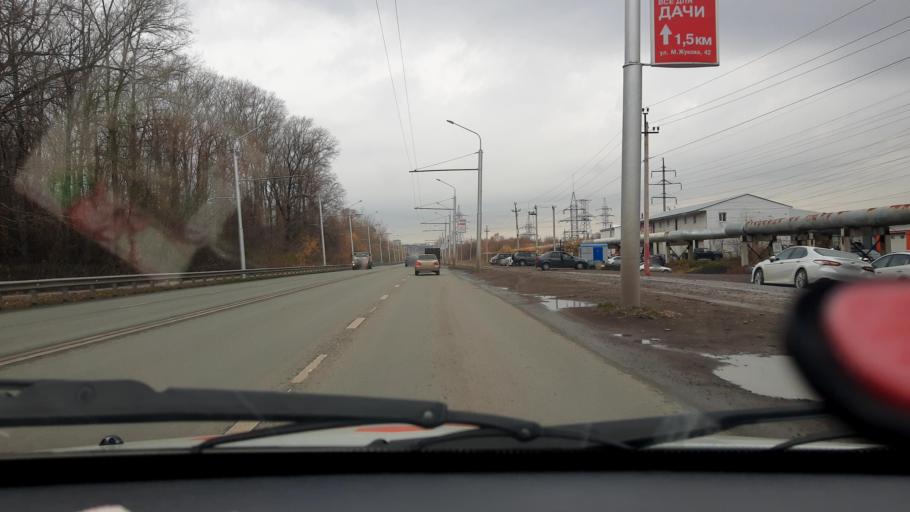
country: RU
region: Bashkortostan
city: Ufa
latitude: 54.7902
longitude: 56.1006
